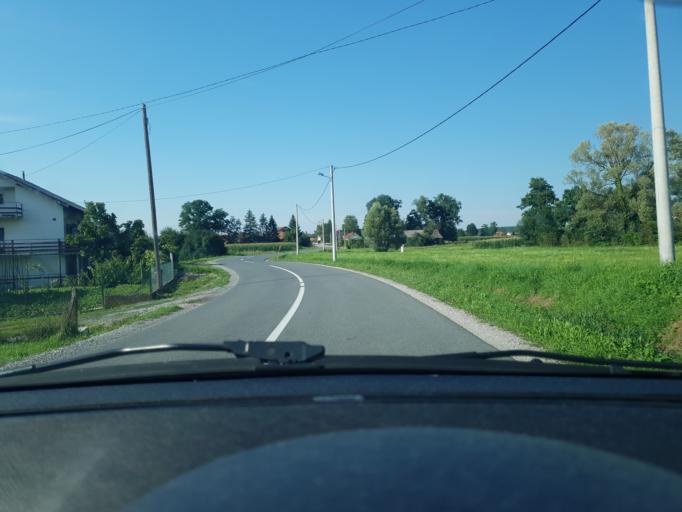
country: HR
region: Zagrebacka
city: Jakovlje
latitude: 45.9376
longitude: 15.8440
